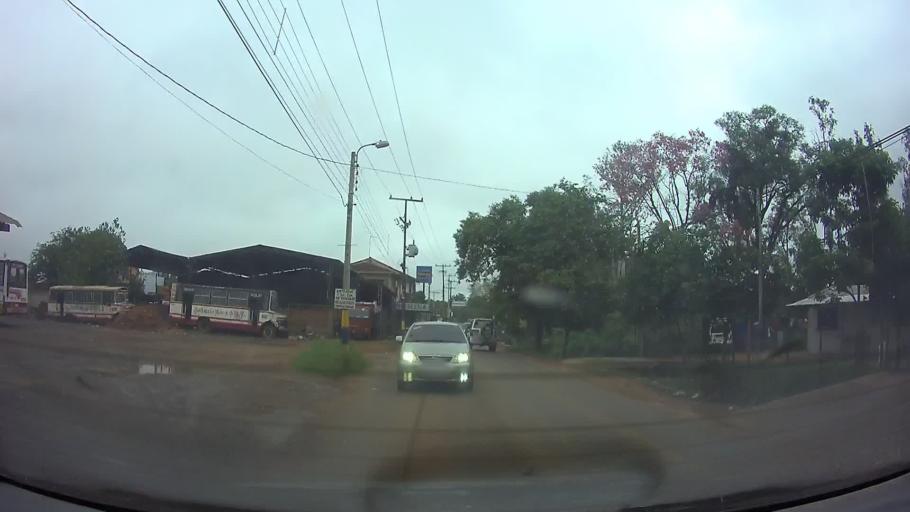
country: PY
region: Central
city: San Lorenzo
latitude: -25.3136
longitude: -57.4929
